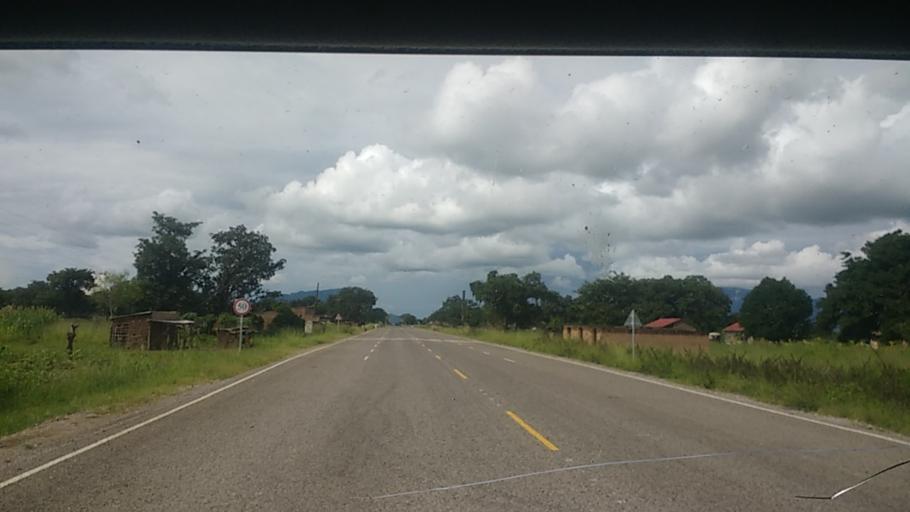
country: UG
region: Eastern Region
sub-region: Katakwi District
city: Katakwi
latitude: 2.0215
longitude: 34.1155
